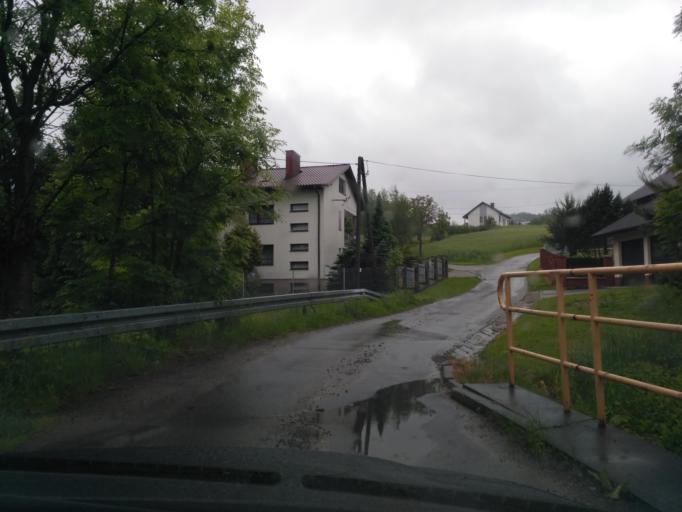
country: PL
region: Lesser Poland Voivodeship
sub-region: Powiat gorlicki
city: Gorlice
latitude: 49.6682
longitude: 21.1398
